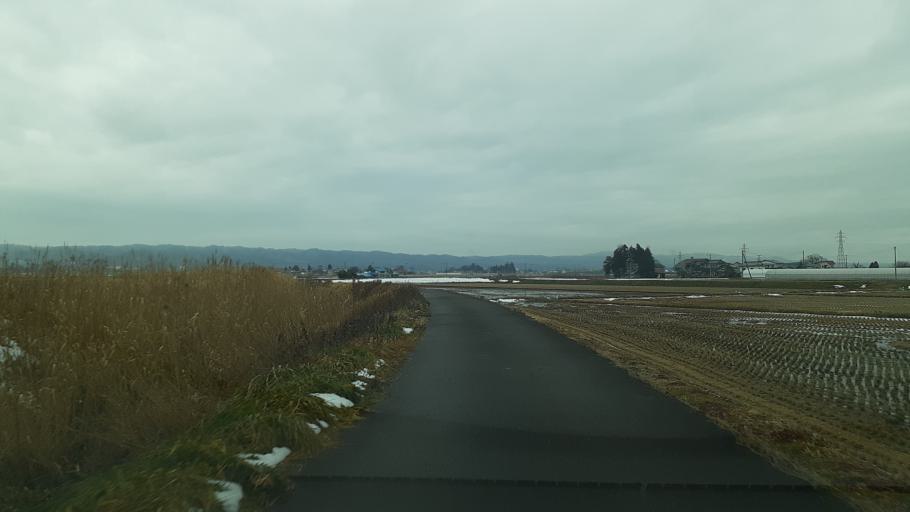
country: JP
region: Fukushima
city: Kitakata
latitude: 37.5420
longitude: 139.8396
